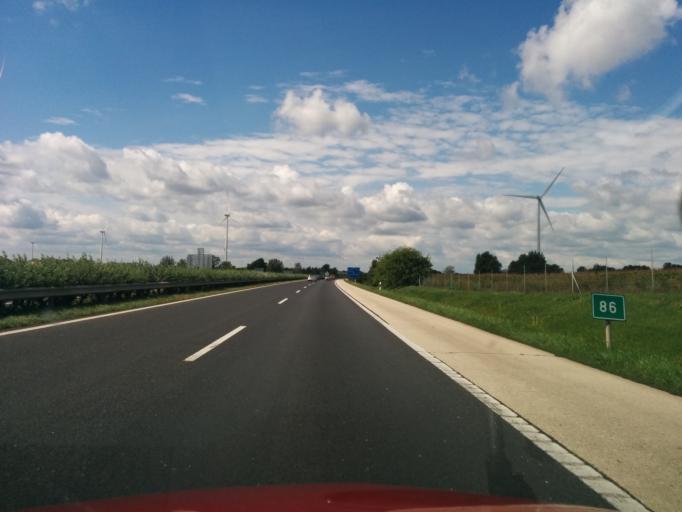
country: HU
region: Komarom-Esztergom
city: Nagyigmand
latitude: 47.6742
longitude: 18.0779
